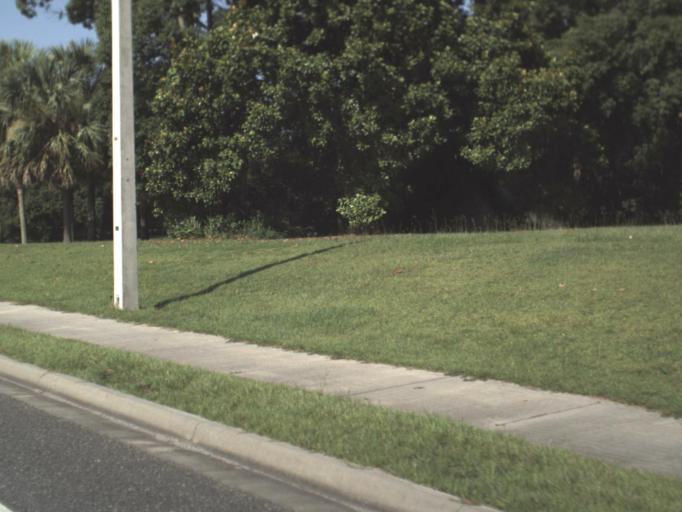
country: US
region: Florida
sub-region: Columbia County
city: Lake City
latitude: 30.1465
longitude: -82.6502
